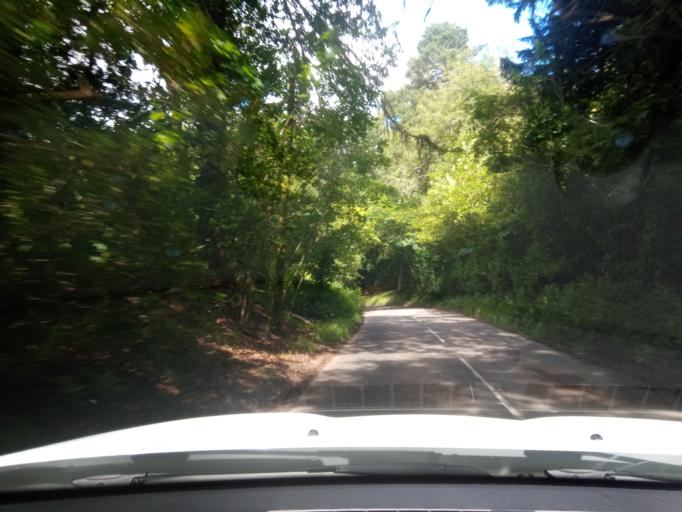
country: GB
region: Scotland
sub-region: The Scottish Borders
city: Selkirk
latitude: 55.5494
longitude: -2.9058
